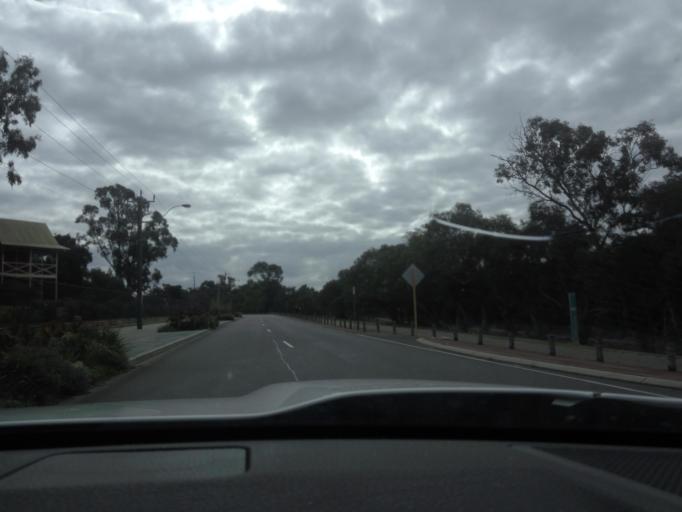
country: AU
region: Western Australia
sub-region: City of Cockburn
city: Bibra Lake
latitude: -32.0949
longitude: 115.8201
